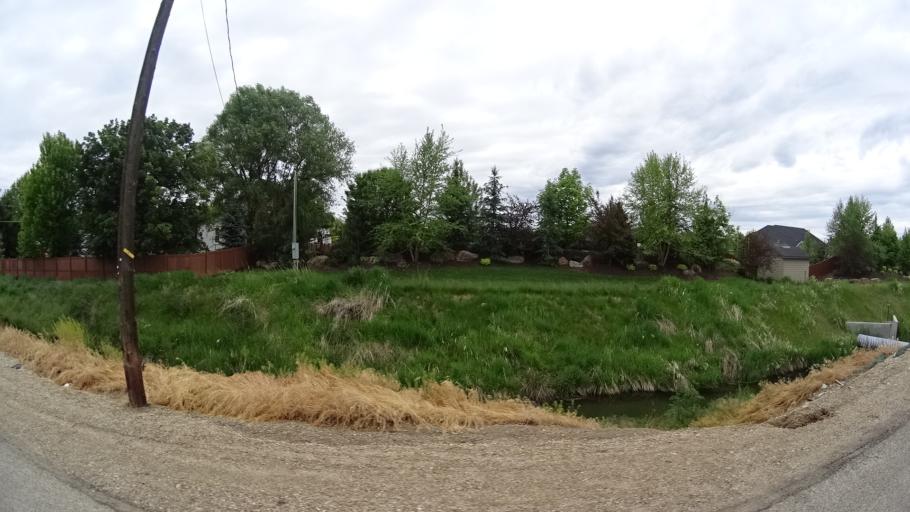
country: US
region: Idaho
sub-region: Ada County
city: Eagle
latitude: 43.7064
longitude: -116.3799
